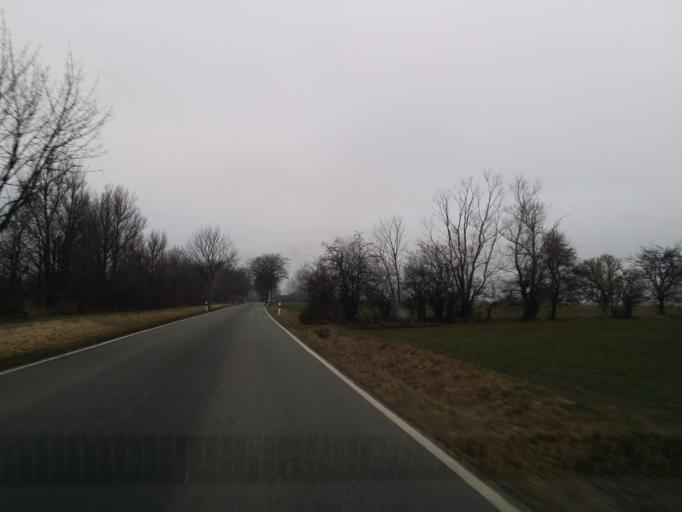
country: DE
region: Schleswig-Holstein
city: Fehmarn
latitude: 54.4601
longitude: 11.1243
